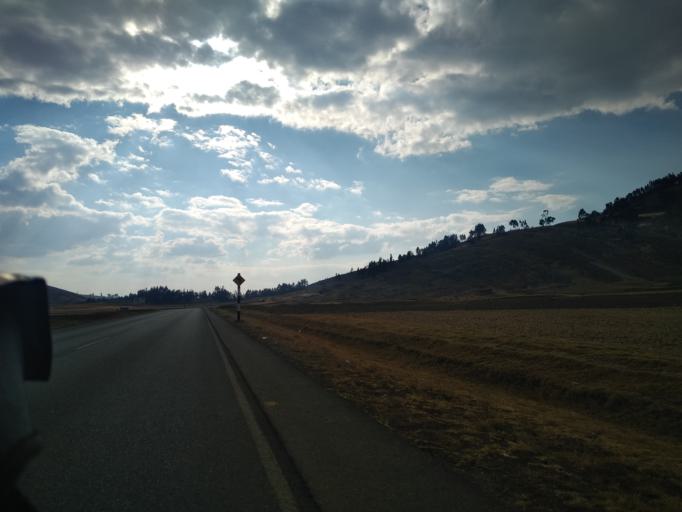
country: PE
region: Cajamarca
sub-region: Provincia de Cajamarca
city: Encanada
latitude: -7.1386
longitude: -78.3847
